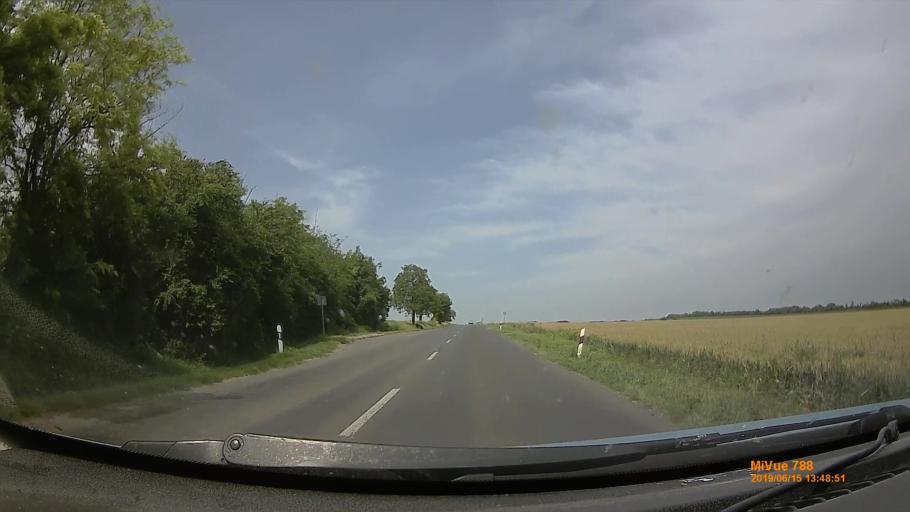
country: HU
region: Tolna
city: Iregszemcse
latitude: 46.7213
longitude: 18.1717
